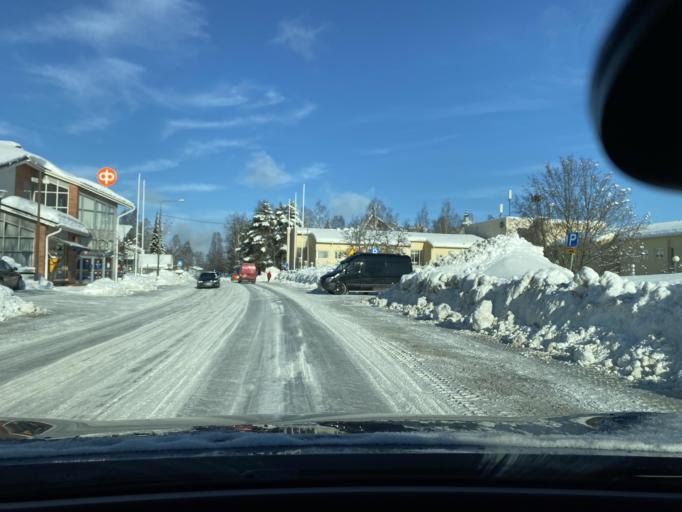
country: FI
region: Southern Savonia
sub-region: Mikkeli
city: Kangasniemi
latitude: 61.9891
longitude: 26.6434
